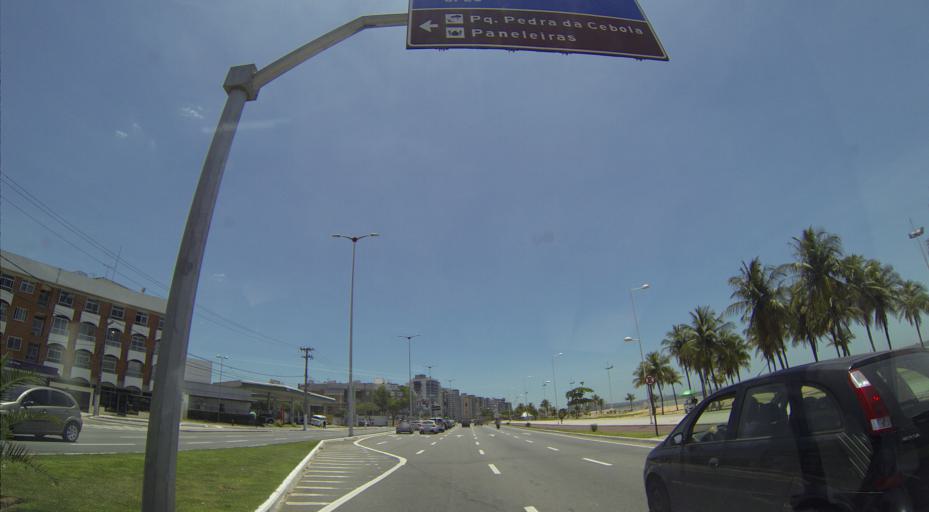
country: BR
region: Espirito Santo
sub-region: Vila Velha
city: Vila Velha
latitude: -20.2842
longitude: -40.2903
